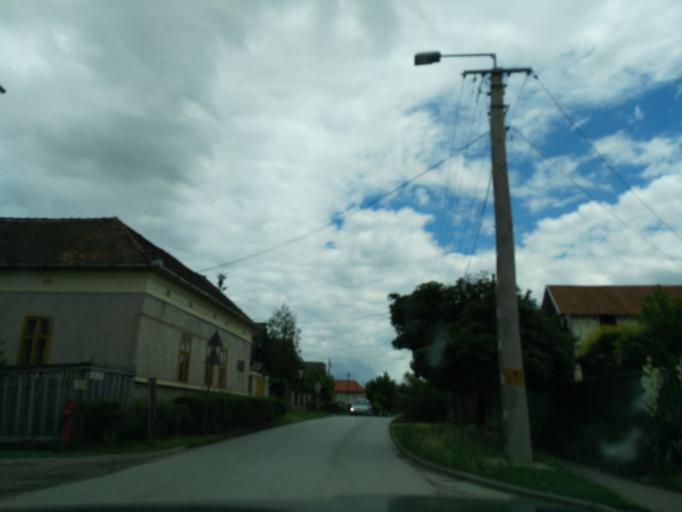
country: HU
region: Hajdu-Bihar
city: Debrecen
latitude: 47.5420
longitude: 21.6483
